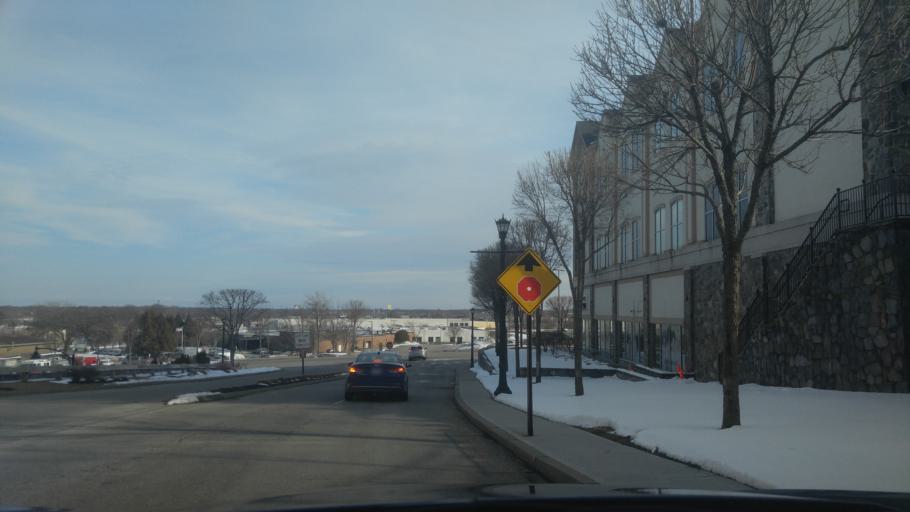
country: US
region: Rhode Island
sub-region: Providence County
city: Cranston
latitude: 41.7557
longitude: -71.4594
